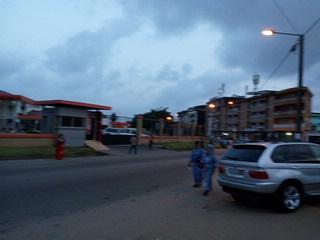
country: CI
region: Lagunes
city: Abidjan
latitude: 5.3441
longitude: -4.0679
